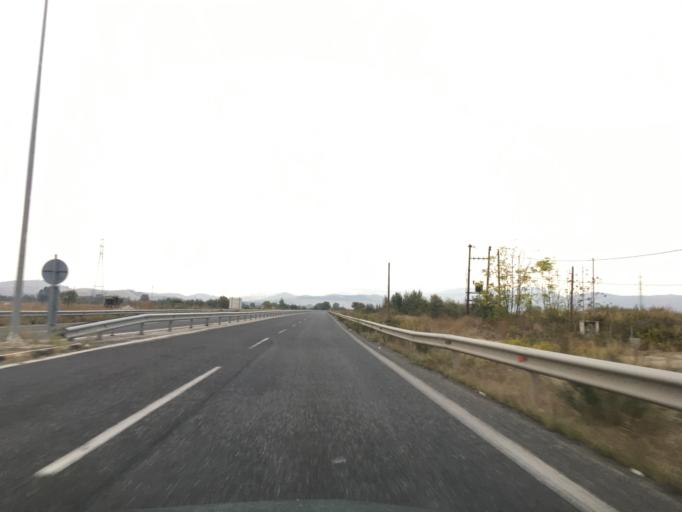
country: GR
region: Thessaly
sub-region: Trikala
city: Trikala
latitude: 39.5578
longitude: 21.8022
